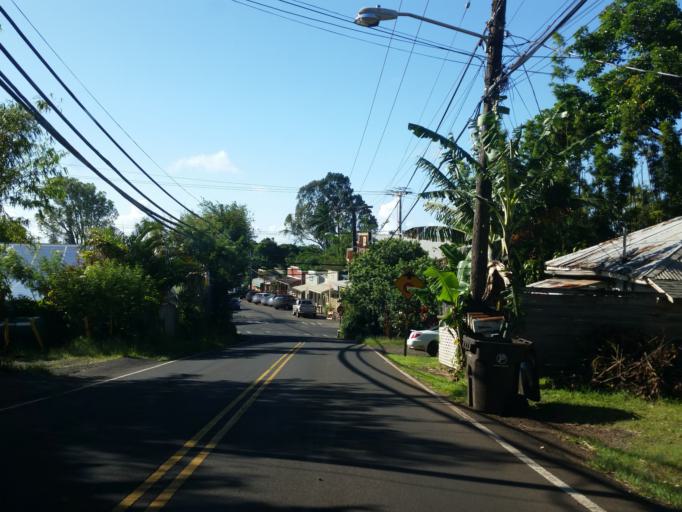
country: US
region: Hawaii
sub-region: Maui County
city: Makawao
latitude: 20.8535
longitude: -156.3100
